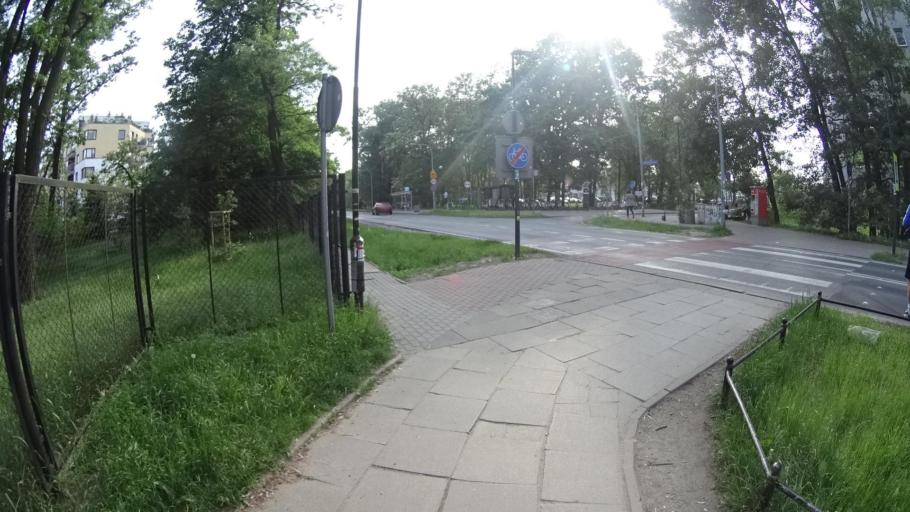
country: PL
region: Masovian Voivodeship
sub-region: Warszawa
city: Bemowo
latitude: 52.2576
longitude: 20.9329
